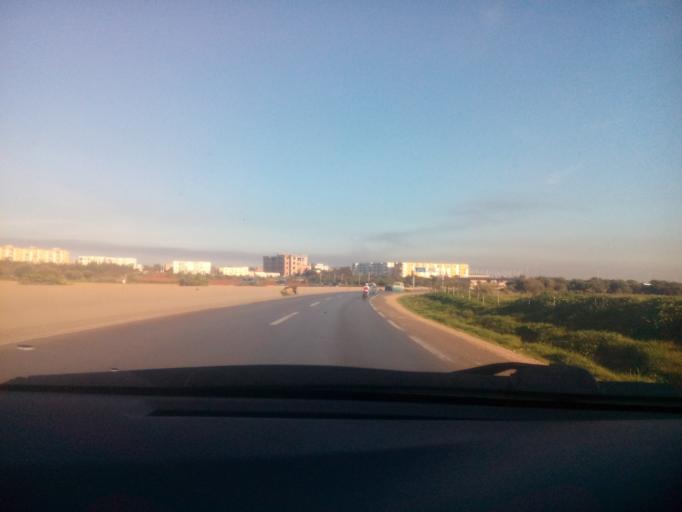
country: DZ
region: Oran
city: Bir el Djir
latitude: 35.7742
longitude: -0.4407
